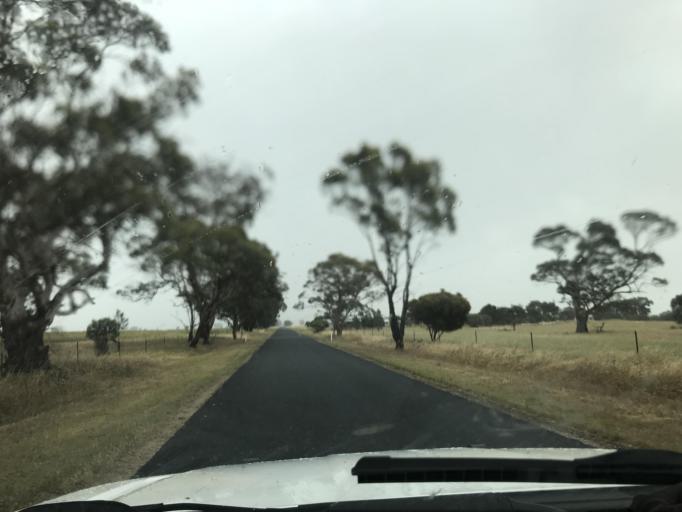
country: AU
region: South Australia
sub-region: Tatiara
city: Bordertown
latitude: -36.3170
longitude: 141.1816
